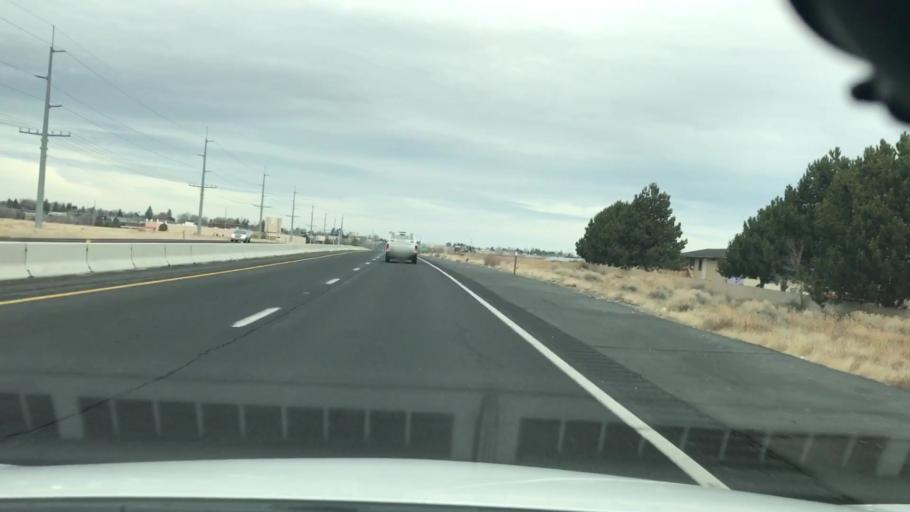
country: US
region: Washington
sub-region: Grant County
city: Moses Lake
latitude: 47.1465
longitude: -119.2861
